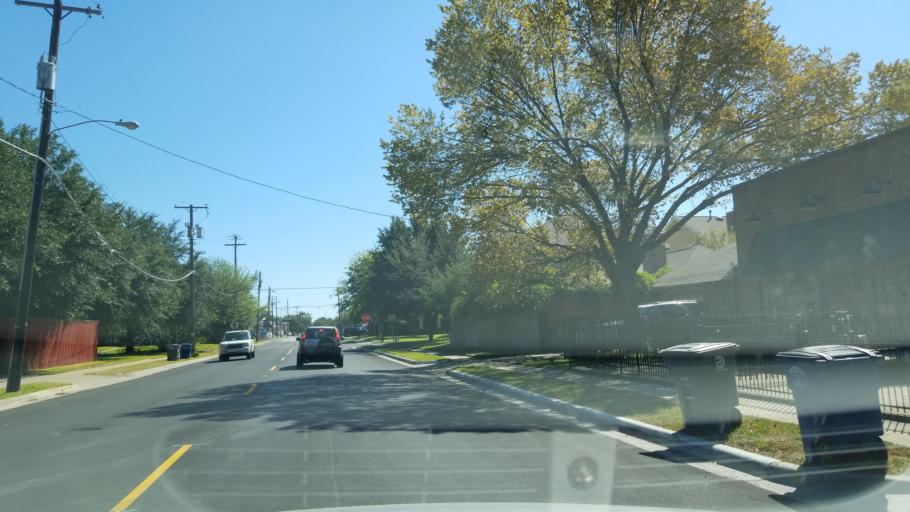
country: US
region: Texas
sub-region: Dallas County
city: Highland Park
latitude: 32.7982
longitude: -96.7639
